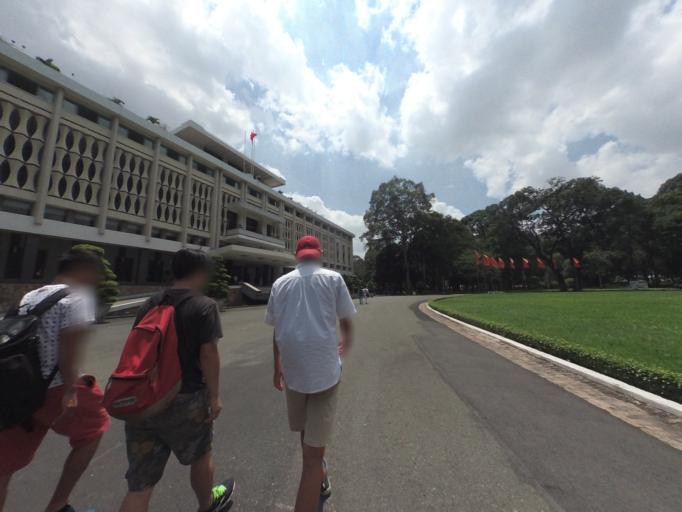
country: VN
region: Ho Chi Minh City
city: Quan Mot
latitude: 10.7772
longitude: 106.6959
